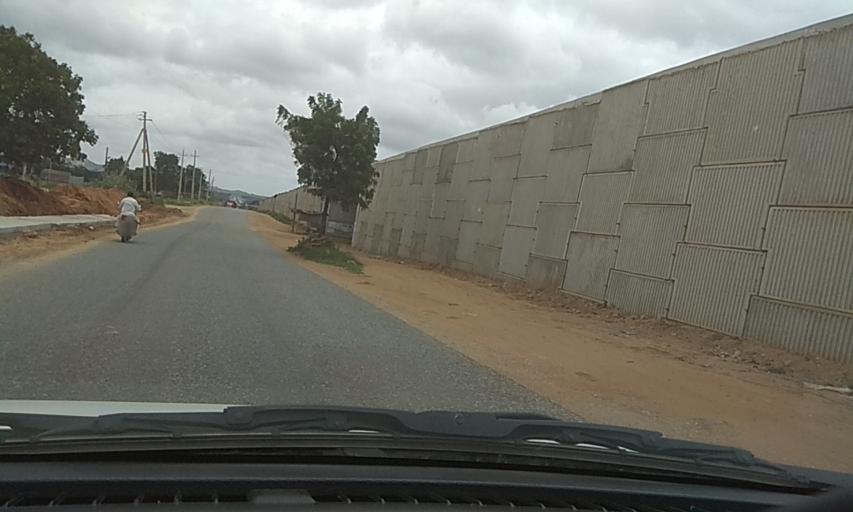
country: IN
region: Karnataka
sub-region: Chitradurga
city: Chitradurga
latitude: 14.2827
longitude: 76.3036
